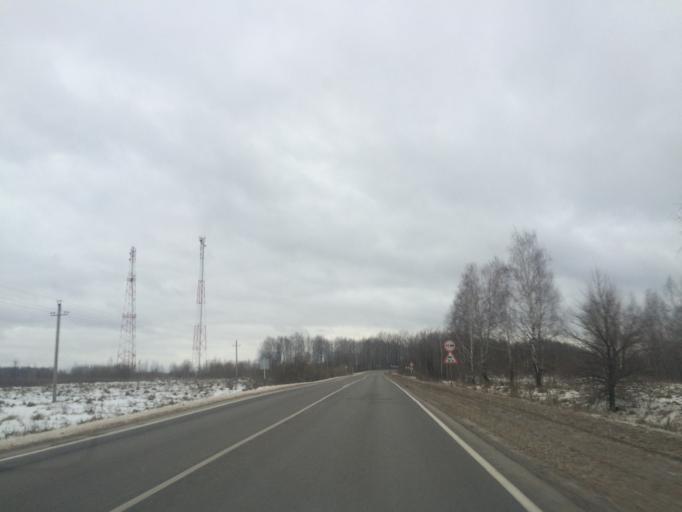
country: RU
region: Tula
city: Leninskiy
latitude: 54.1322
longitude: 37.2994
